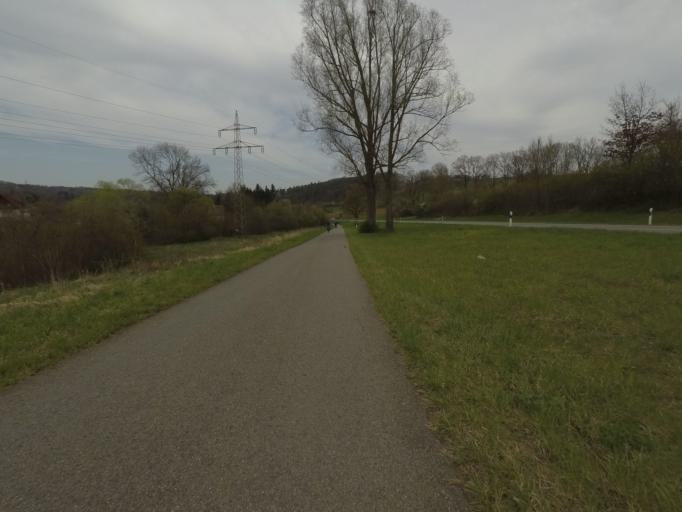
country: DE
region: Baden-Wuerttemberg
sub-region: Tuebingen Region
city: Dusslingen
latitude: 48.4665
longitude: 9.0719
